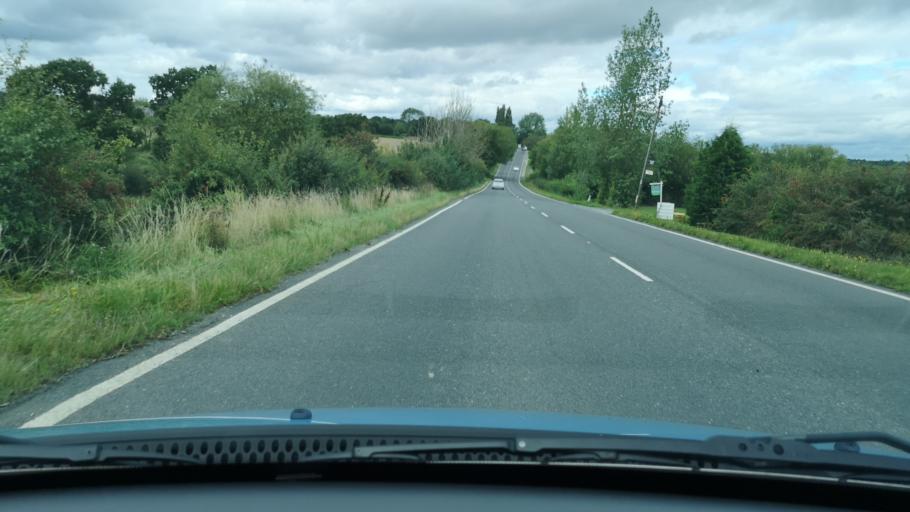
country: GB
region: England
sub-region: City and Borough of Wakefield
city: Low Ackworth
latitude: 53.6362
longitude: -1.3270
